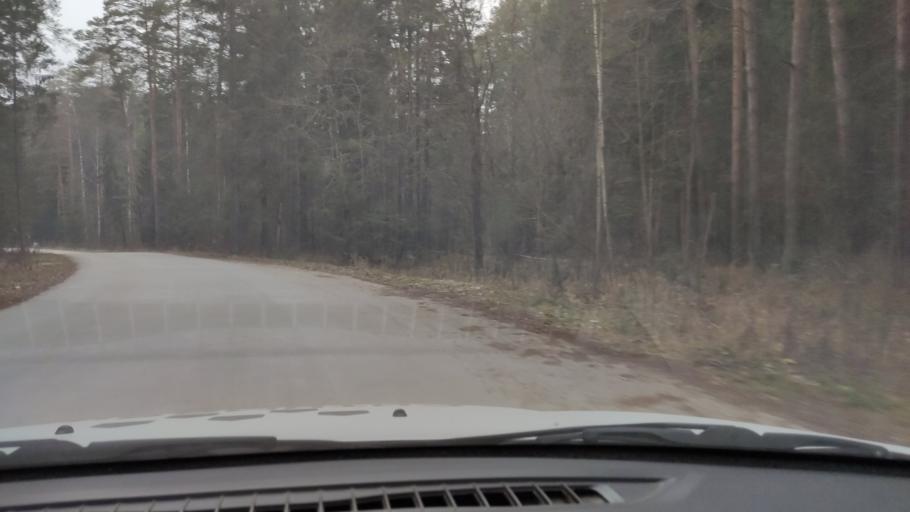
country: RU
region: Perm
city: Kondratovo
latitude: 58.0472
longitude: 56.1485
